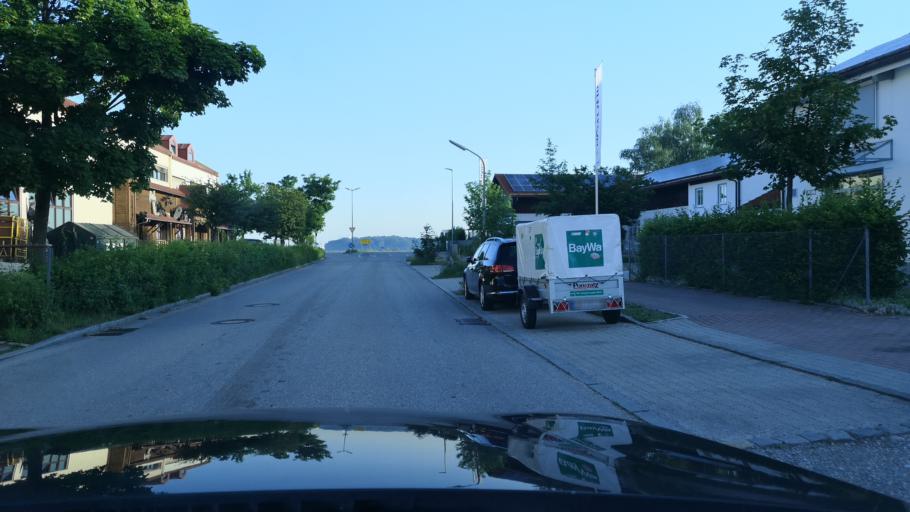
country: DE
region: Bavaria
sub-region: Upper Bavaria
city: Kirchheim bei Muenchen
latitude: 48.1828
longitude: 11.7701
